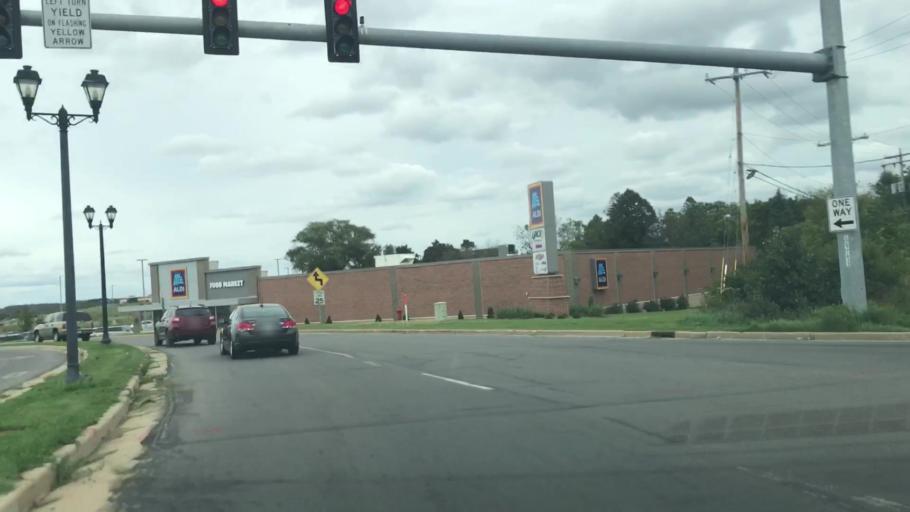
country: US
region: Wisconsin
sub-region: Waukesha County
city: Mukwonago
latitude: 42.8486
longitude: -88.3183
